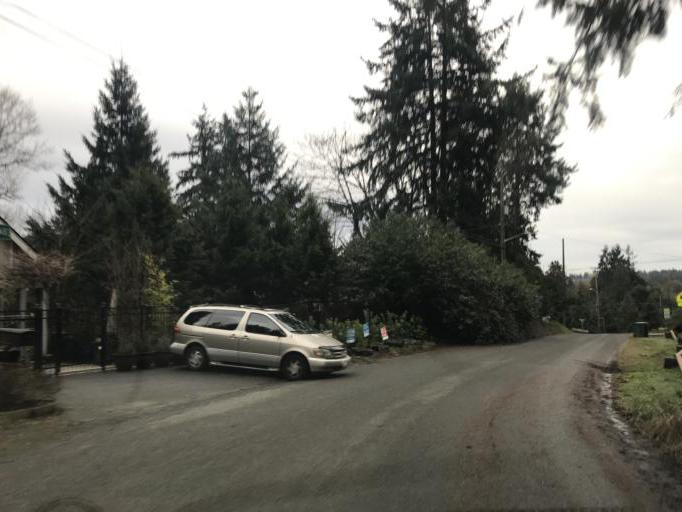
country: US
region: Washington
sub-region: King County
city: Lake Forest Park
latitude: 47.7129
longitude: -122.2932
